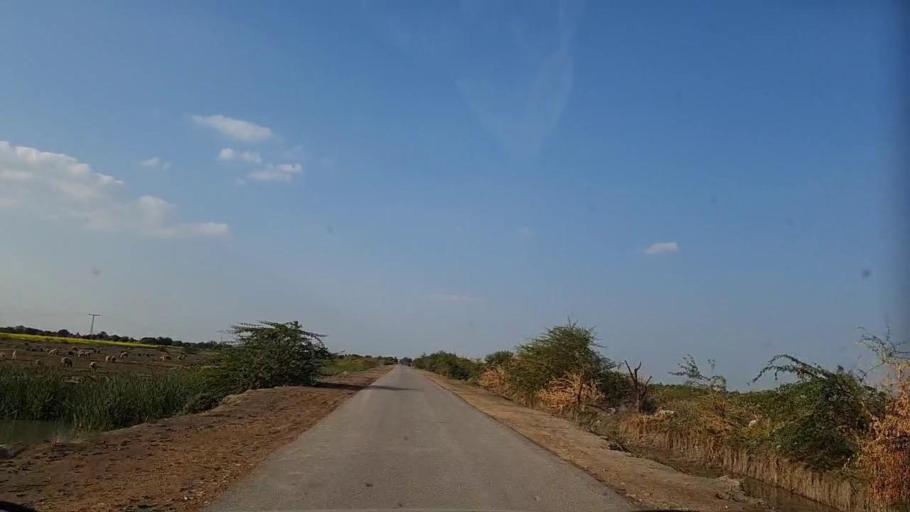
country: PK
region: Sindh
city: Pithoro
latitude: 25.7181
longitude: 69.2179
